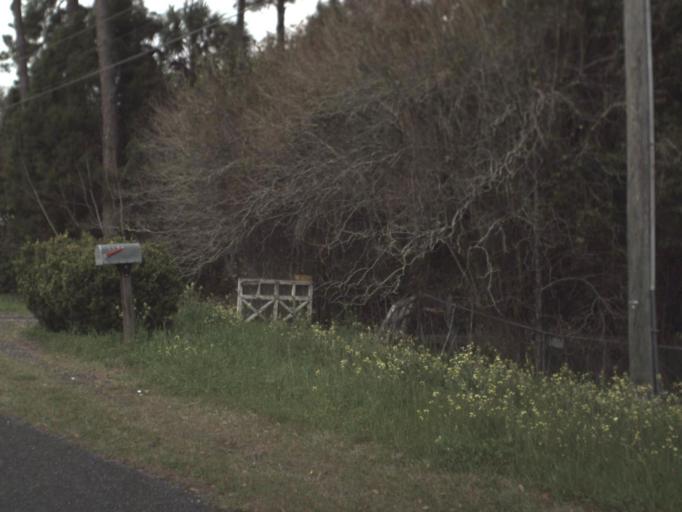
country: US
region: Florida
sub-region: Leon County
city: Tallahassee
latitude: 30.4263
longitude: -84.1833
